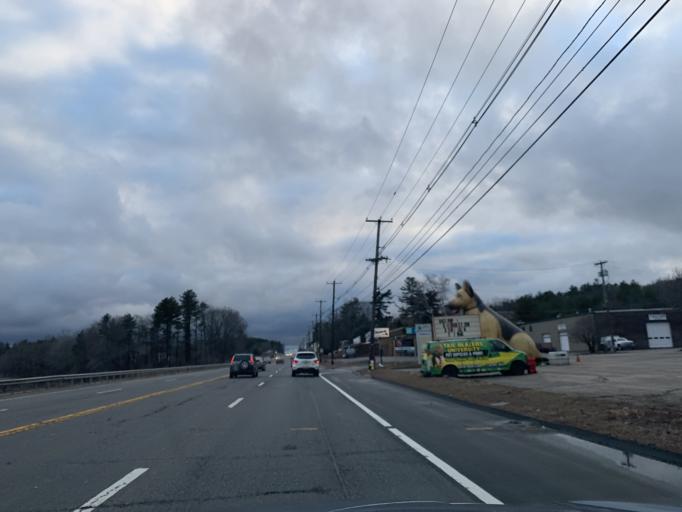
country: US
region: Massachusetts
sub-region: Norfolk County
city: Wrentham
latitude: 42.0518
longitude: -71.3001
